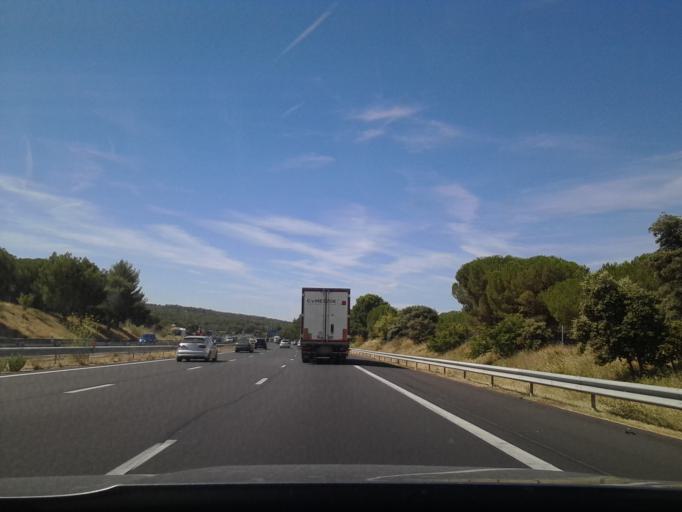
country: FR
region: Languedoc-Roussillon
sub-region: Departement de l'Aude
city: Vinassan
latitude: 43.2203
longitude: 3.0938
